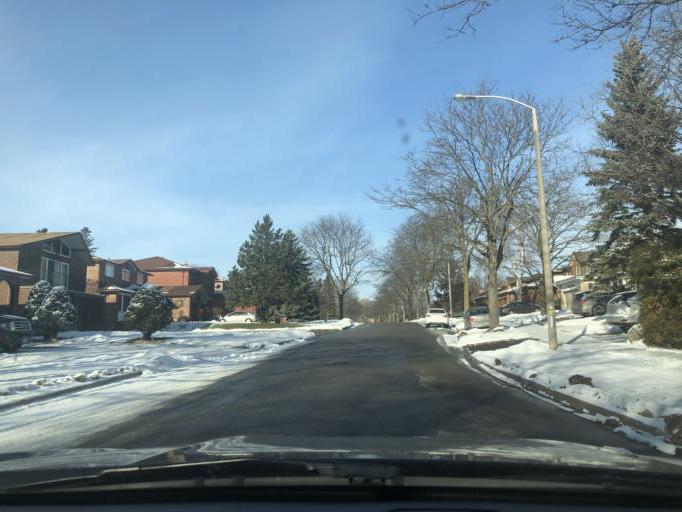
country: CA
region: Ontario
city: Scarborough
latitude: 43.7875
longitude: -79.1522
